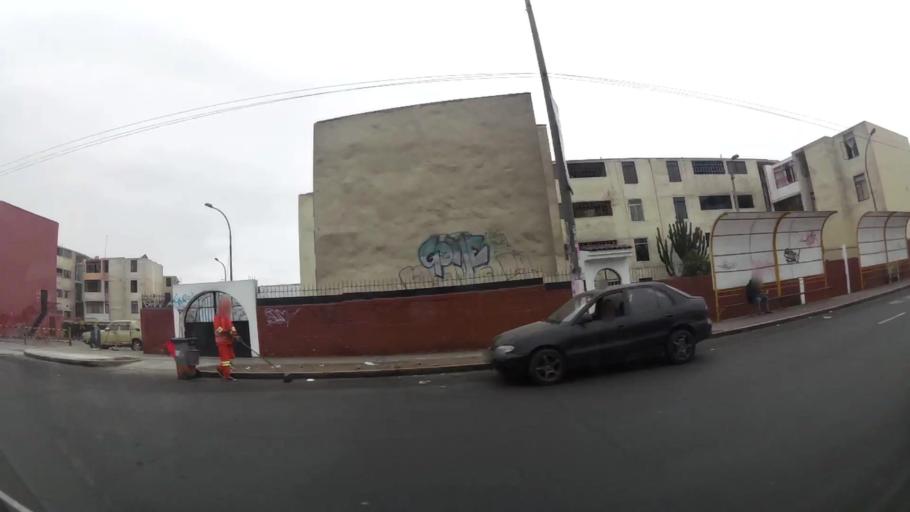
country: PE
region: Callao
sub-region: Callao
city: Callao
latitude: -12.0592
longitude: -77.0743
